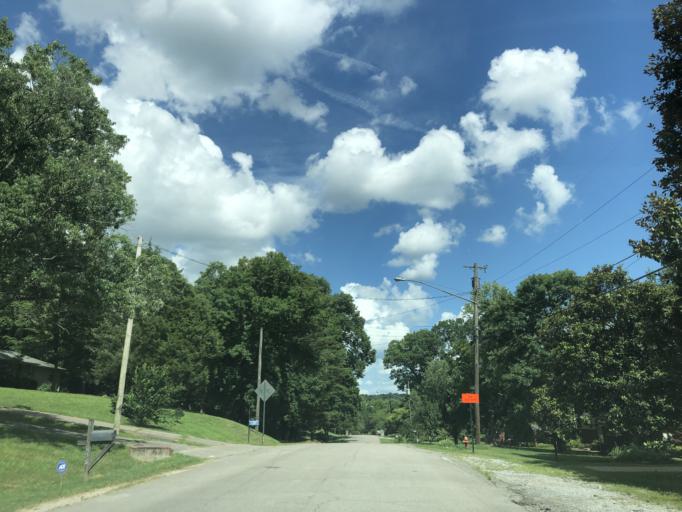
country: US
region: Tennessee
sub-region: Davidson County
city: Oak Hill
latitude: 36.0794
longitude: -86.7362
